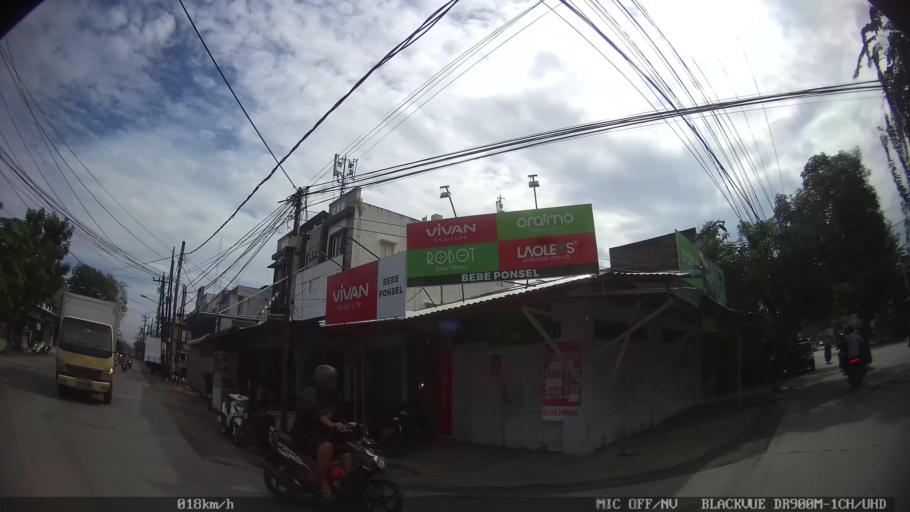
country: ID
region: North Sumatra
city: Sunggal
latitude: 3.6066
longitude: 98.6122
